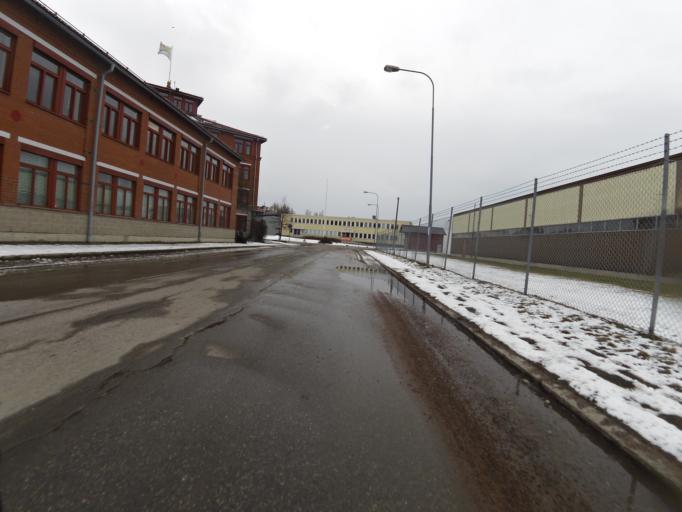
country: SE
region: Gaevleborg
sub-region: Gavle Kommun
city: Gavle
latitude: 60.6818
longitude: 17.1568
